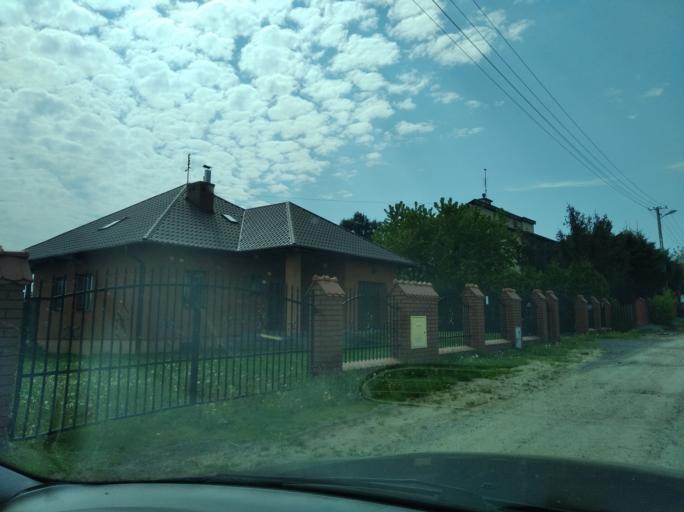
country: PL
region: Subcarpathian Voivodeship
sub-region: Powiat jaroslawski
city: Jaroslaw
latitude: 50.0012
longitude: 22.6804
